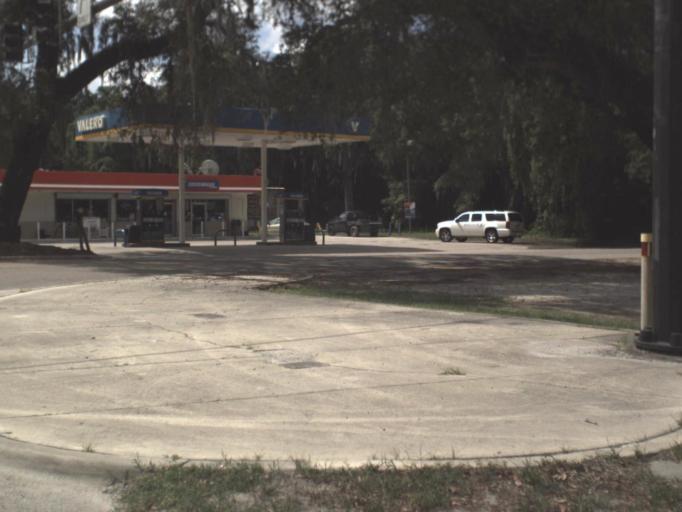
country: US
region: Florida
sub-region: Clay County
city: Green Cove Springs
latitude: 30.0085
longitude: -81.6133
